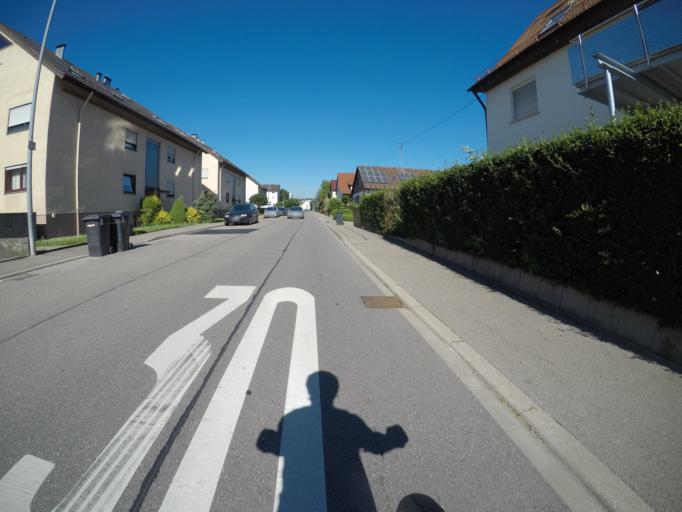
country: DE
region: Baden-Wuerttemberg
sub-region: Regierungsbezirk Stuttgart
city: Ehningen
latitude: 48.6571
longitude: 8.9405
